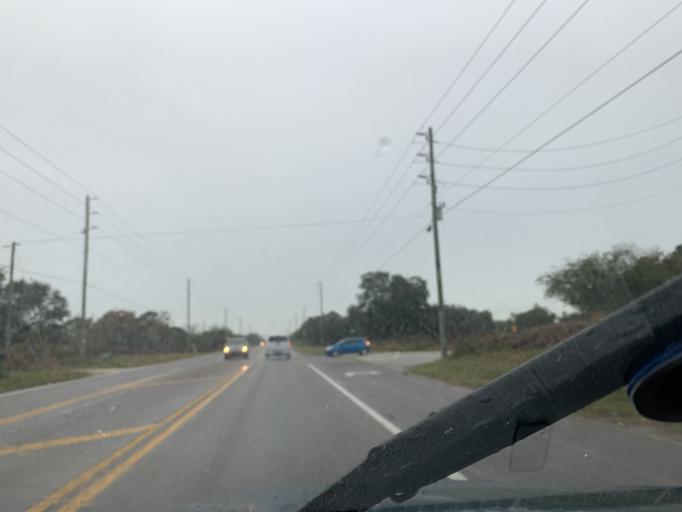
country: US
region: Florida
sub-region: Pasco County
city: Shady Hills
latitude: 28.4338
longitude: -82.5079
